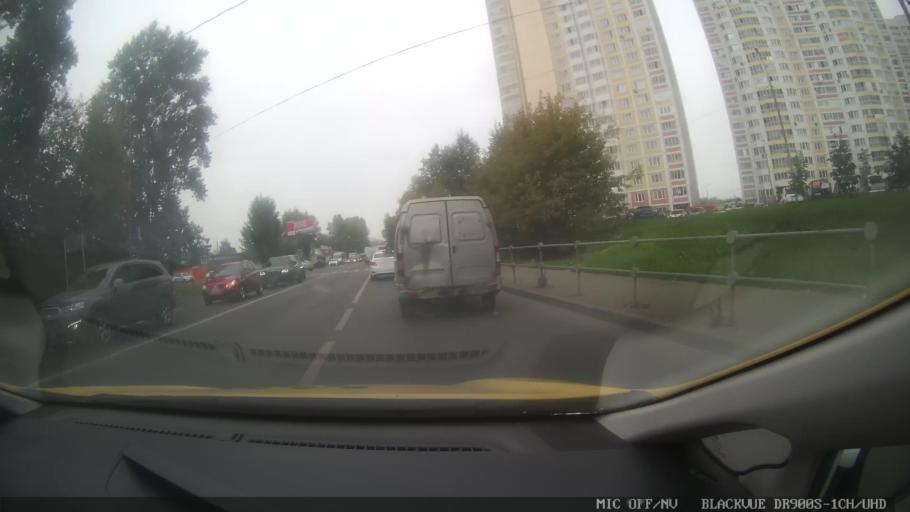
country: RU
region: Moscow
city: Nekrasovka
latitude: 55.6836
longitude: 37.9108
